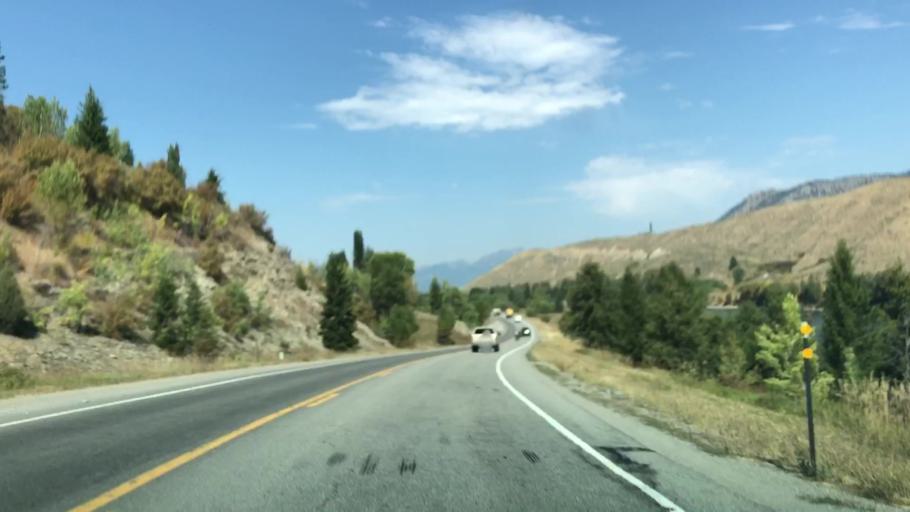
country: US
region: Wyoming
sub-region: Teton County
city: South Park
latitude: 43.3595
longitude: -110.7258
